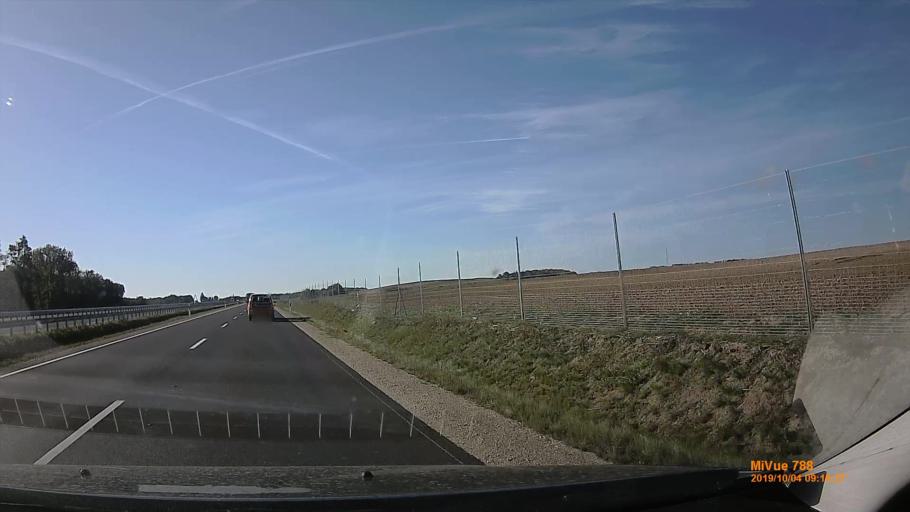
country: HU
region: Somogy
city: Karad
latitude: 46.6129
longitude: 17.7971
